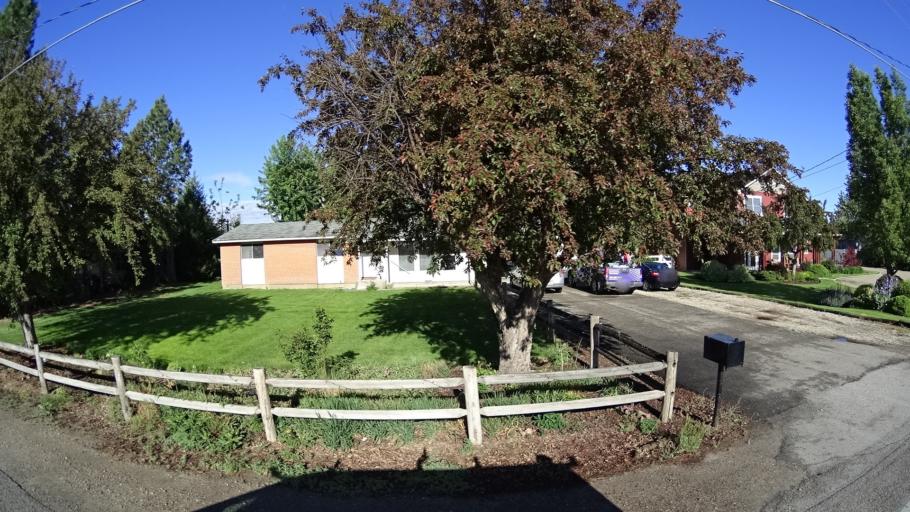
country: US
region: Idaho
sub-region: Ada County
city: Kuna
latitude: 43.4951
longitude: -116.4137
